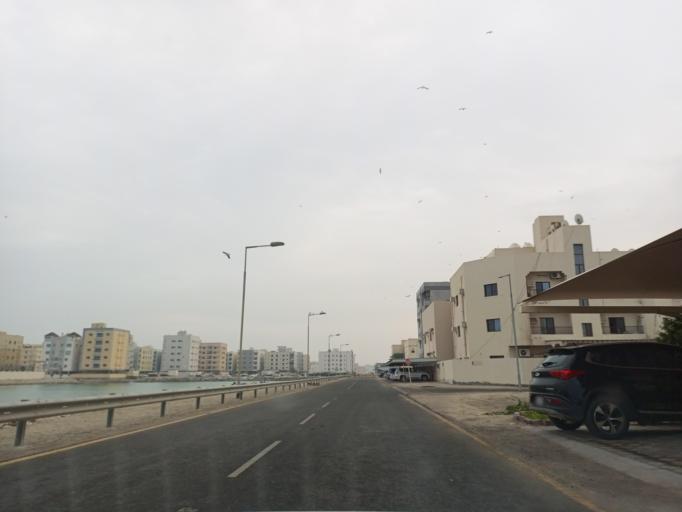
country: BH
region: Muharraq
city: Al Hadd
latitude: 26.2441
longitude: 50.6442
